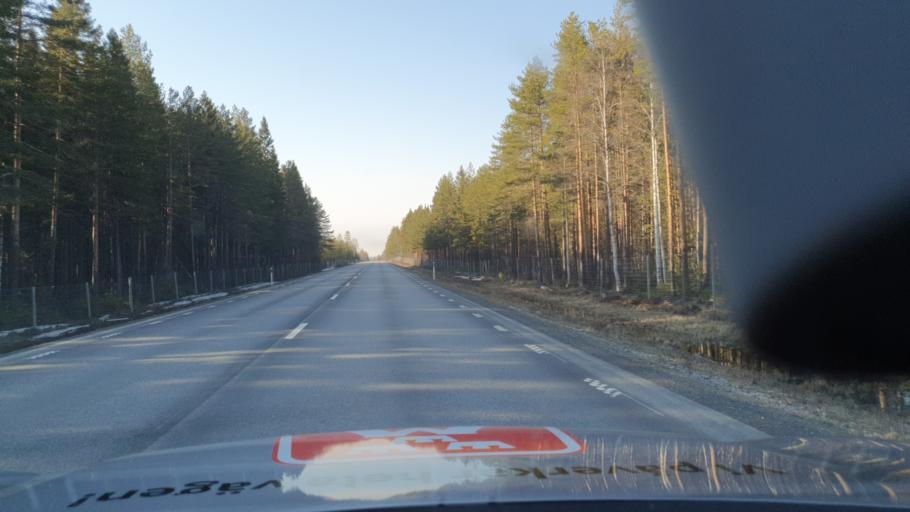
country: SE
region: Vaesterbotten
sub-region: Skelleftea Kommun
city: Burea
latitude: 64.5749
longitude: 21.2239
